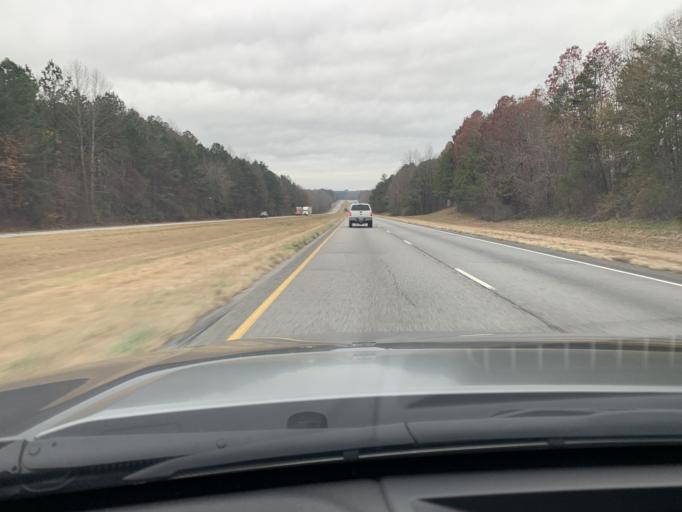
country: US
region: Georgia
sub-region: Habersham County
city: Raoul
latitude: 34.4344
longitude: -83.6345
